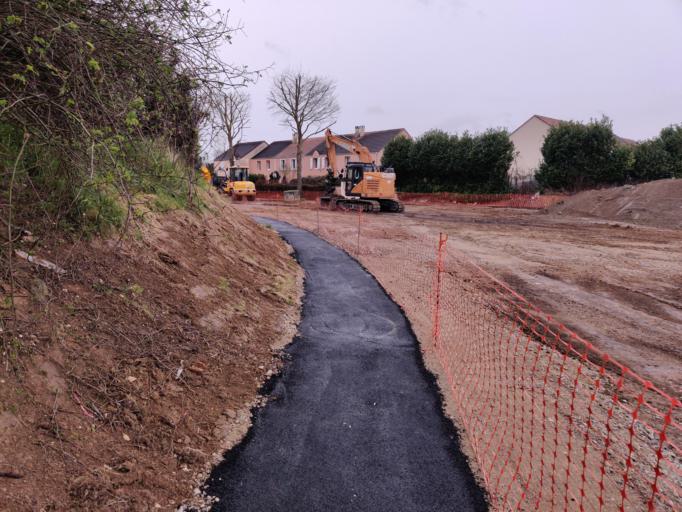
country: FR
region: Ile-de-France
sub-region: Departement du Val-d'Oise
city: Fontenay-en-Parisis
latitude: 49.0302
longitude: 2.4478
